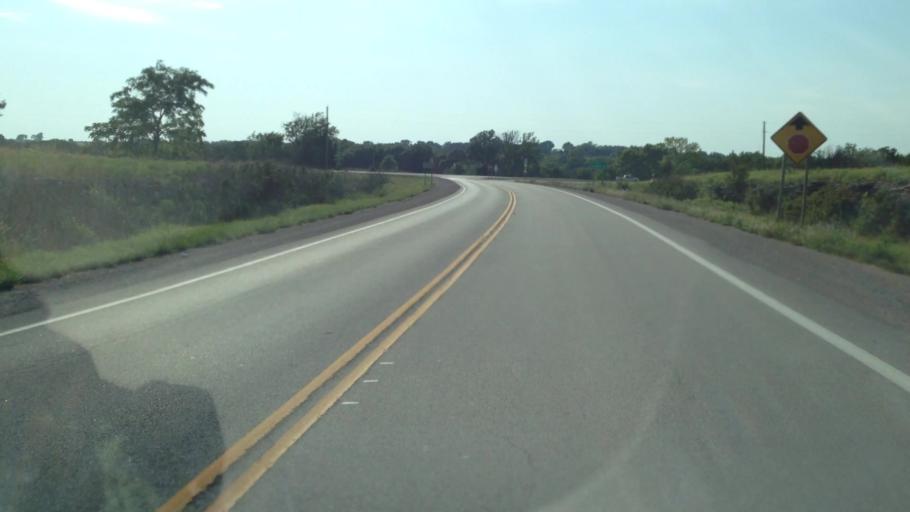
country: US
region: Kansas
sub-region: Anderson County
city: Garnett
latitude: 38.1967
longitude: -95.2480
